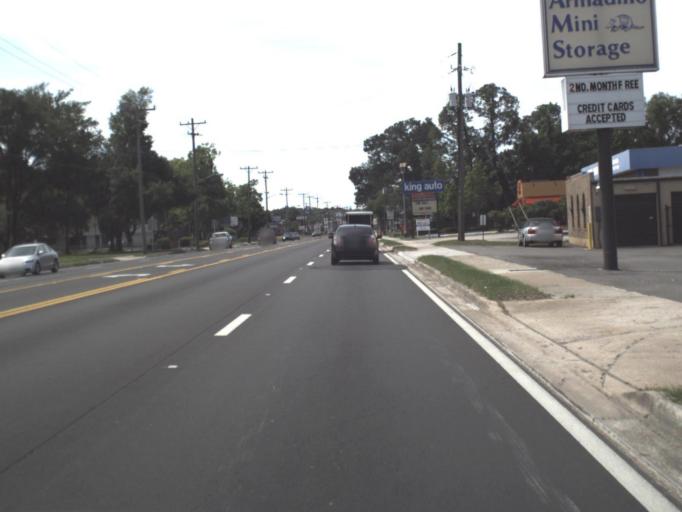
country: US
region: Florida
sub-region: Duval County
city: Jacksonville
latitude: 30.2834
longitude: -81.6028
